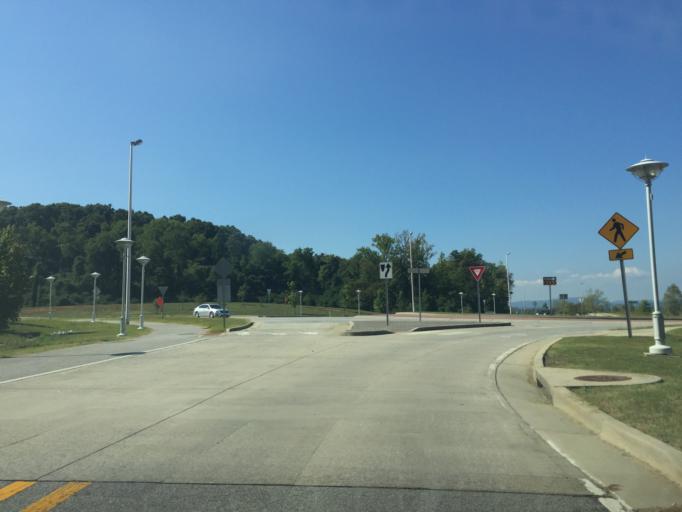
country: US
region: Tennessee
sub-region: Hamilton County
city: Harrison
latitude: 35.0767
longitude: -85.1266
